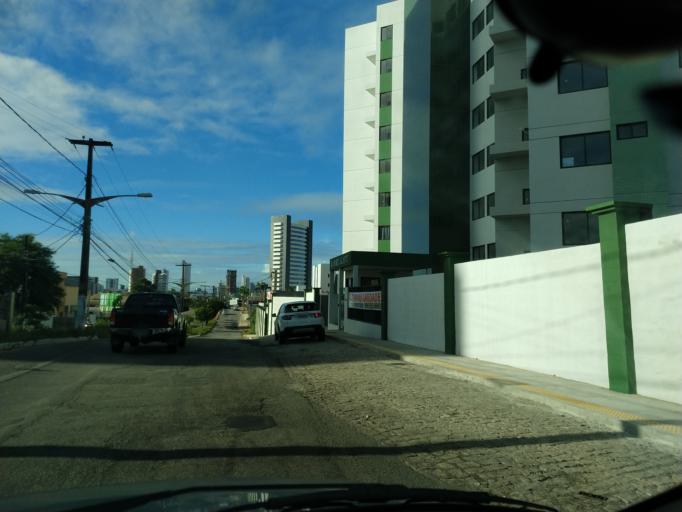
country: BR
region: Rio Grande do Norte
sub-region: Natal
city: Natal
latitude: -5.8377
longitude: -35.2256
